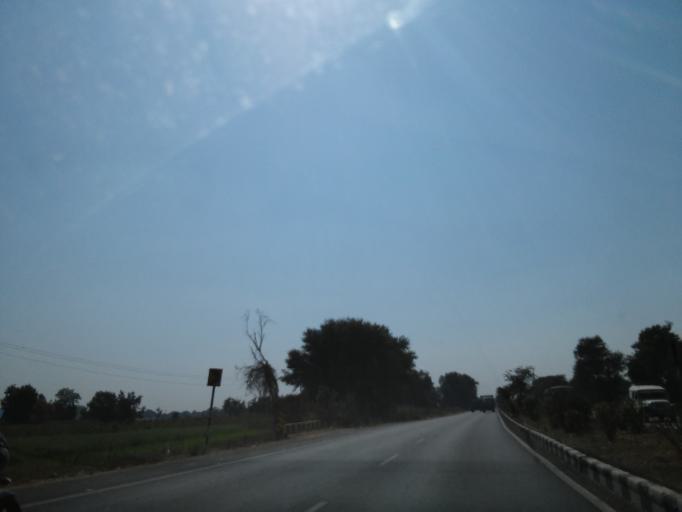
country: IN
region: Gujarat
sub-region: Gandhinagar
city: Chhala
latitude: 23.3215
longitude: 72.7788
